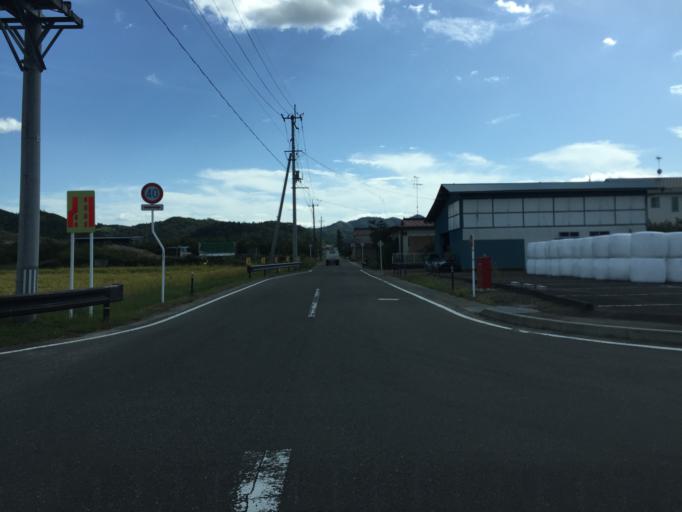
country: JP
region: Fukushima
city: Hobaramachi
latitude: 37.8107
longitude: 140.5727
